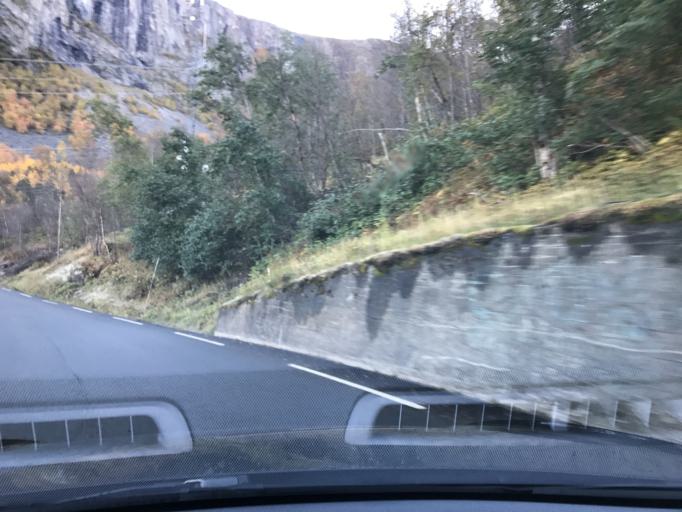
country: NO
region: Sogn og Fjordane
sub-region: Aurland
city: Aurlandsvangen
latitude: 60.8551
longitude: 7.3067
